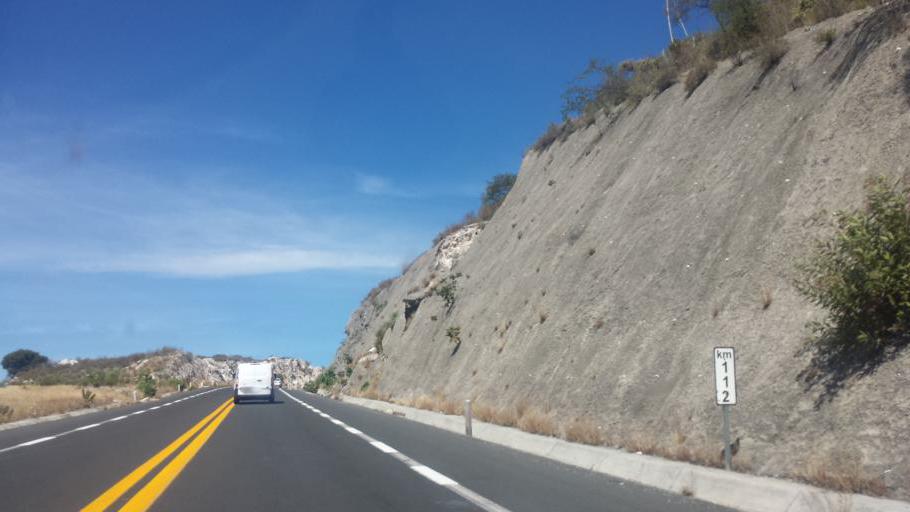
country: MX
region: Oaxaca
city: San Gabriel Casa Blanca
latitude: 17.9880
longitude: -97.3542
